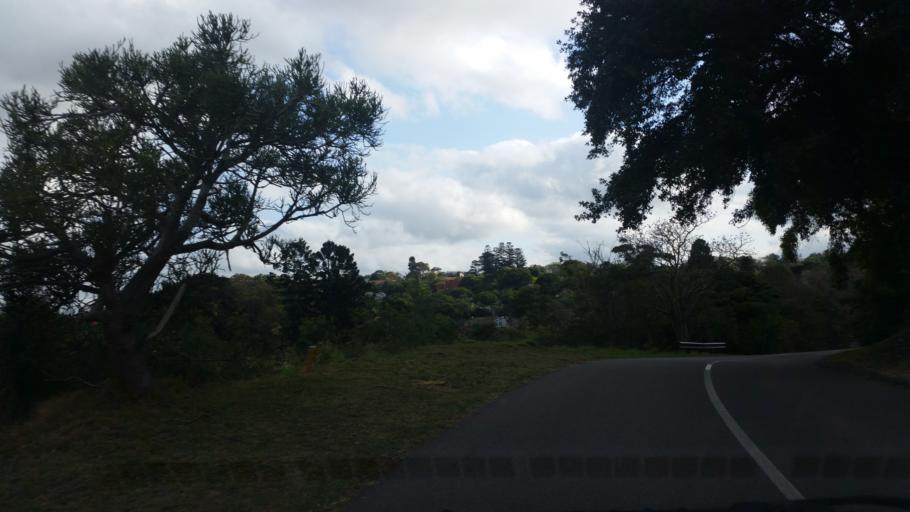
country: ZA
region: KwaZulu-Natal
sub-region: eThekwini Metropolitan Municipality
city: Berea
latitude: -29.8333
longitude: 30.9380
